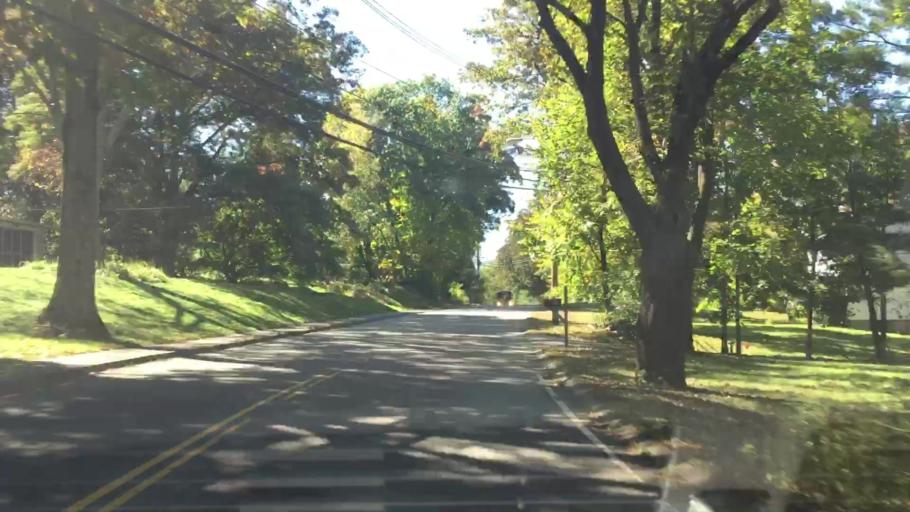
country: US
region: Massachusetts
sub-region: Essex County
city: North Andover
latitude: 42.6818
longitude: -71.0913
